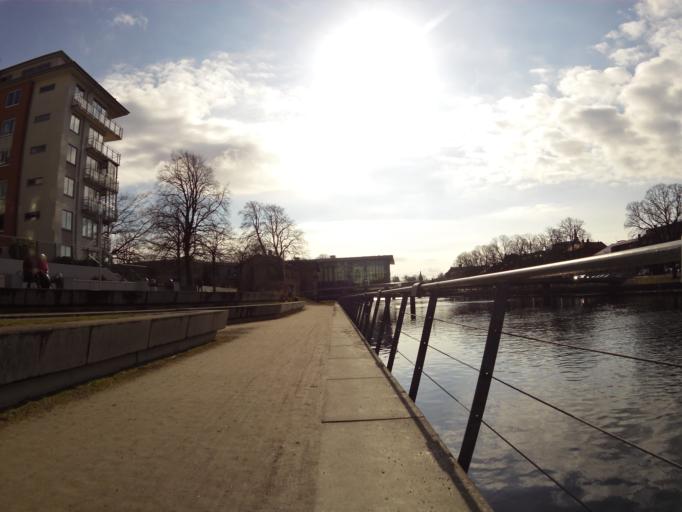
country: SE
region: Halland
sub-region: Halmstads Kommun
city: Halmstad
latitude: 56.6768
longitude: 12.8618
